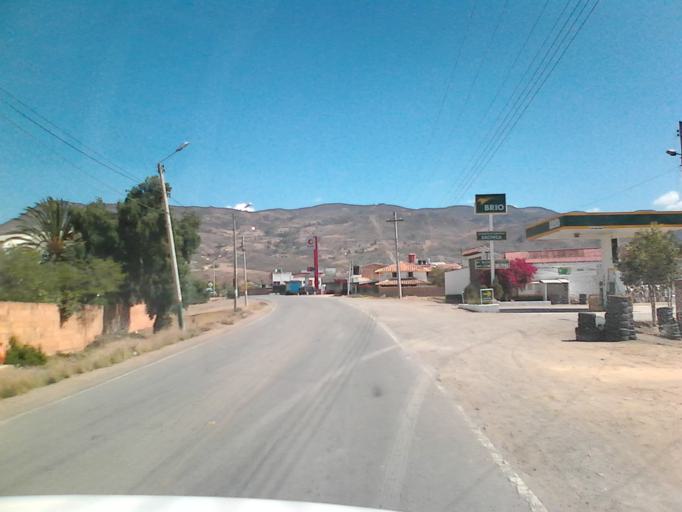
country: CO
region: Boyaca
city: Sachica
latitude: 5.5873
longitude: -73.5416
